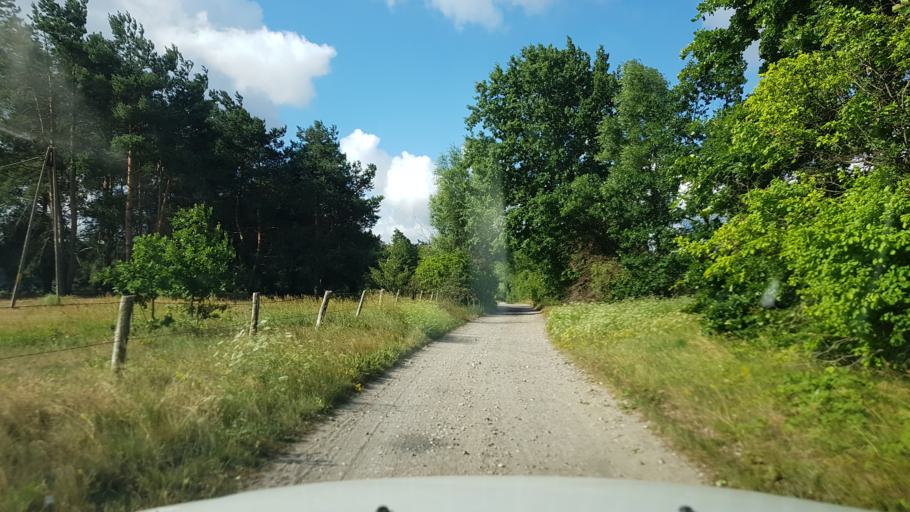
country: PL
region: West Pomeranian Voivodeship
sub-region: Powiat mysliborski
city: Debno
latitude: 52.7281
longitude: 14.6631
